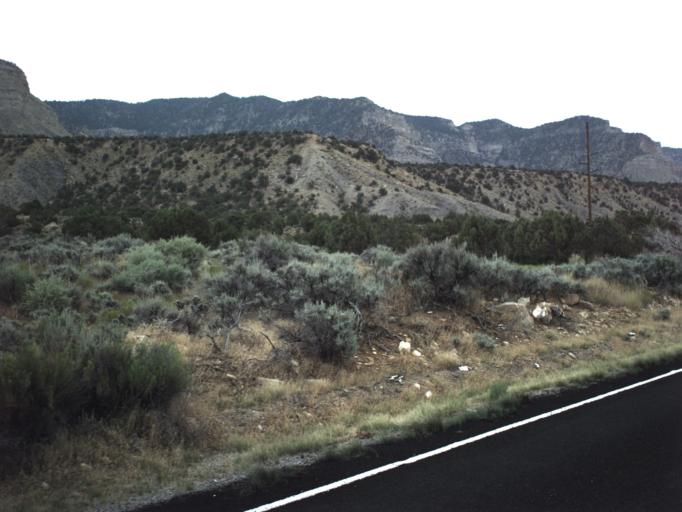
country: US
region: Utah
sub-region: Carbon County
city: East Carbon City
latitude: 39.5174
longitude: -110.3922
